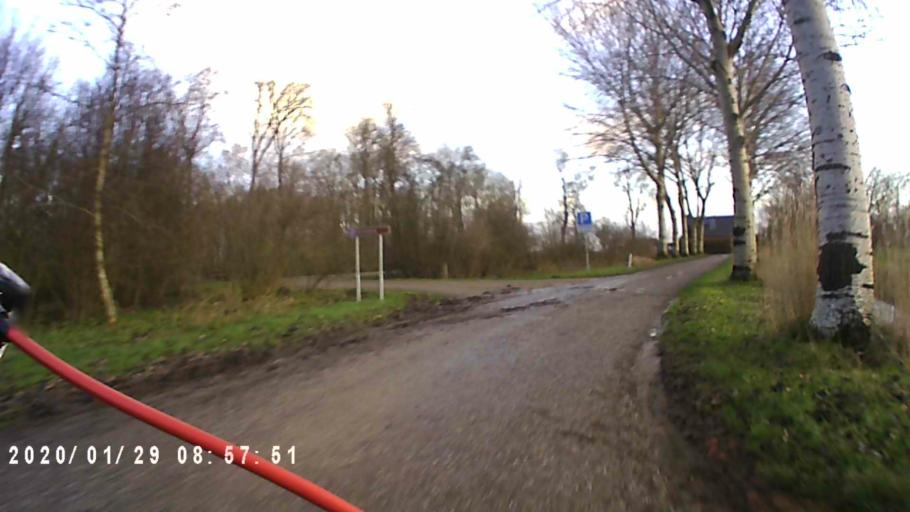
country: NL
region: Groningen
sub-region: Gemeente Zuidhorn
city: Oldehove
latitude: 53.3176
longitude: 6.4540
